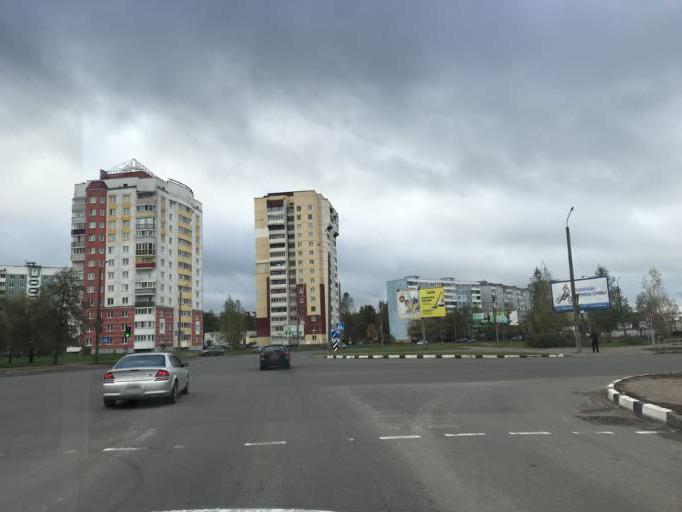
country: BY
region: Mogilev
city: Mahilyow
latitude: 53.8801
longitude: 30.3689
